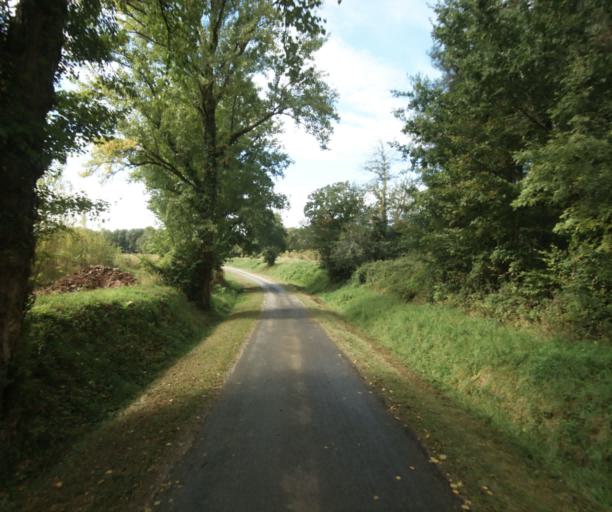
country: FR
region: Aquitaine
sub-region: Departement des Landes
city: Villeneuve-de-Marsan
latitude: 43.8973
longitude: -0.2074
